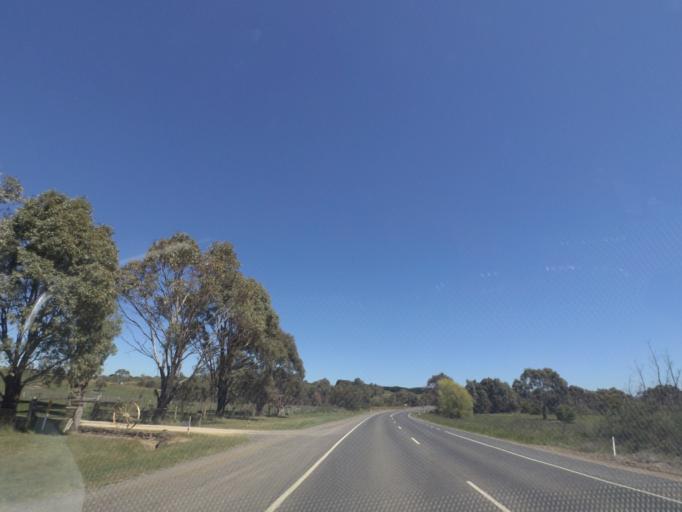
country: AU
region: Victoria
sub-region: Hume
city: Sunbury
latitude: -37.2861
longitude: 144.7804
